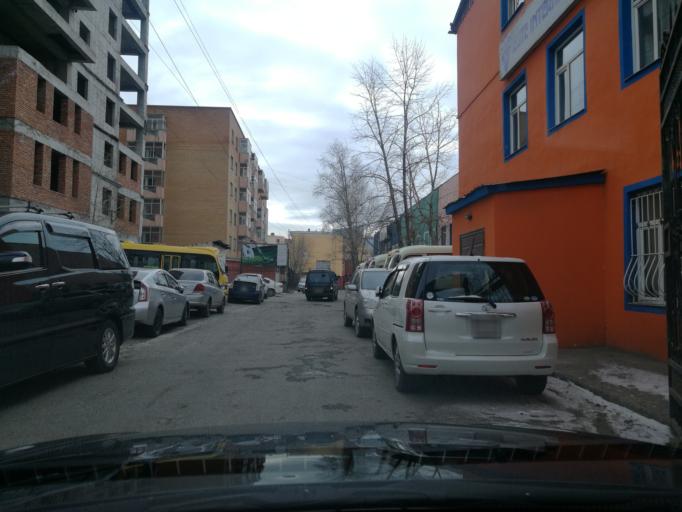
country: MN
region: Ulaanbaatar
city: Ulaanbaatar
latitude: 47.9128
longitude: 106.9111
